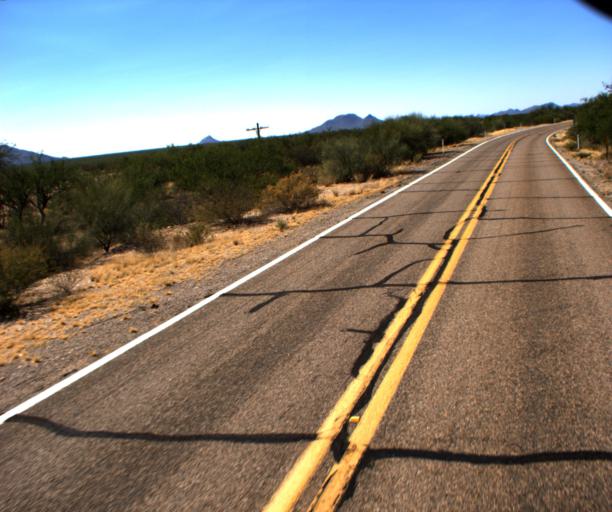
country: US
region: Arizona
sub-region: Pima County
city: Three Points
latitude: 31.9409
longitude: -111.3909
